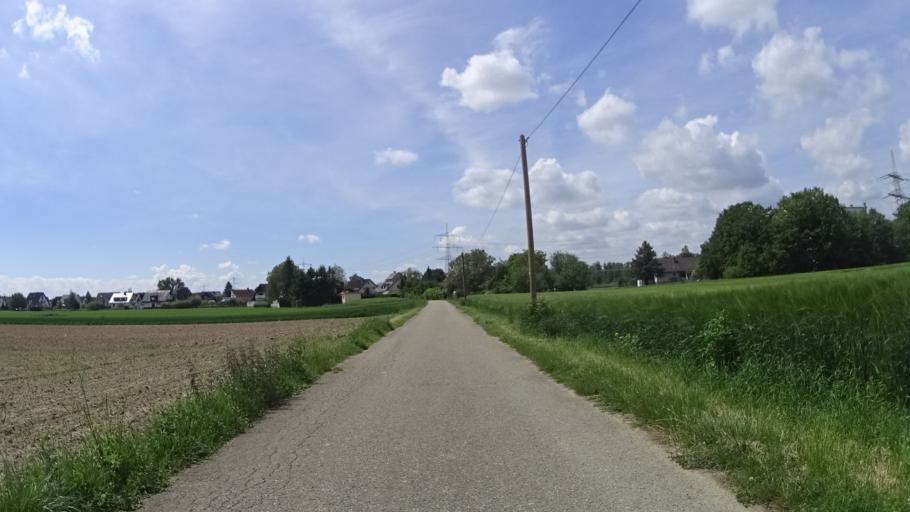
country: DE
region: Baden-Wuerttemberg
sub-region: Freiburg Region
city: Schwanau
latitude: 48.3557
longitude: 7.7547
